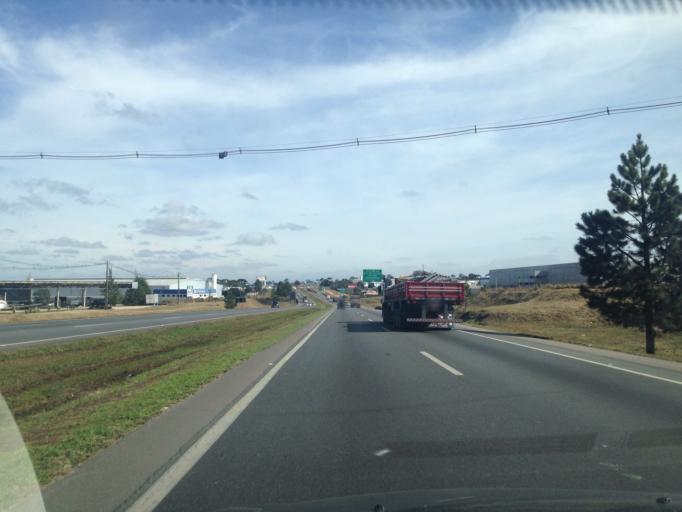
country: BR
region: Parana
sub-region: Sao Jose Dos Pinhais
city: Sao Jose dos Pinhais
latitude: -25.5655
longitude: -49.1636
